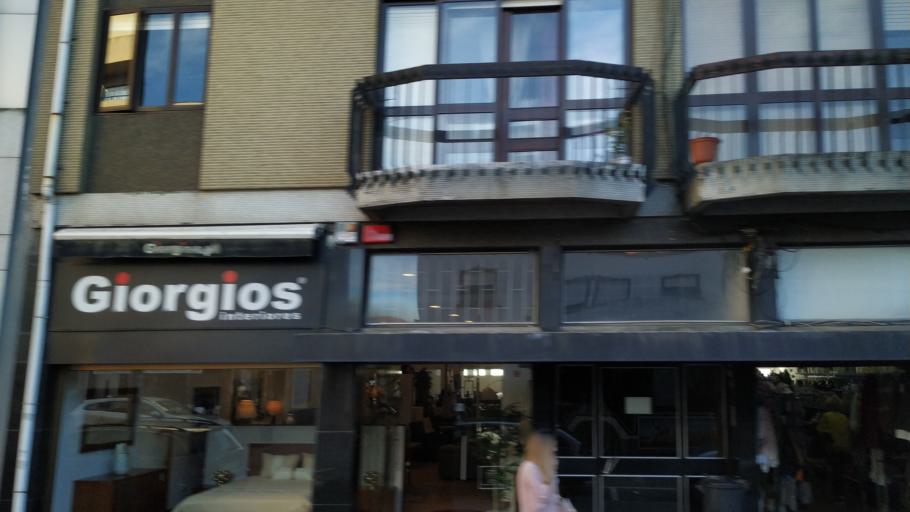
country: PT
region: Porto
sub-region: Vila Nova de Gaia
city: Vilar de Andorinho
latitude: 41.1164
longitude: -8.6076
